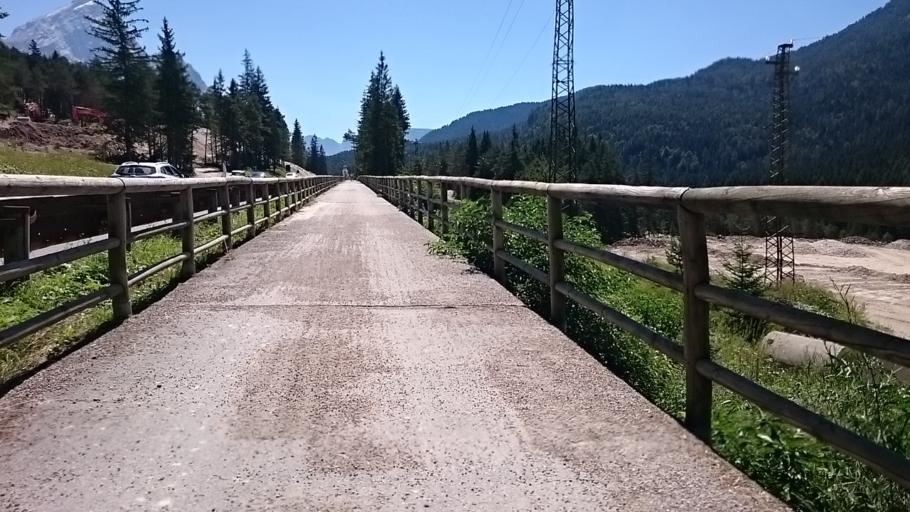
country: IT
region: Veneto
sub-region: Provincia di Belluno
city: Cortina d'Ampezzo
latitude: 46.5030
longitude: 12.1636
